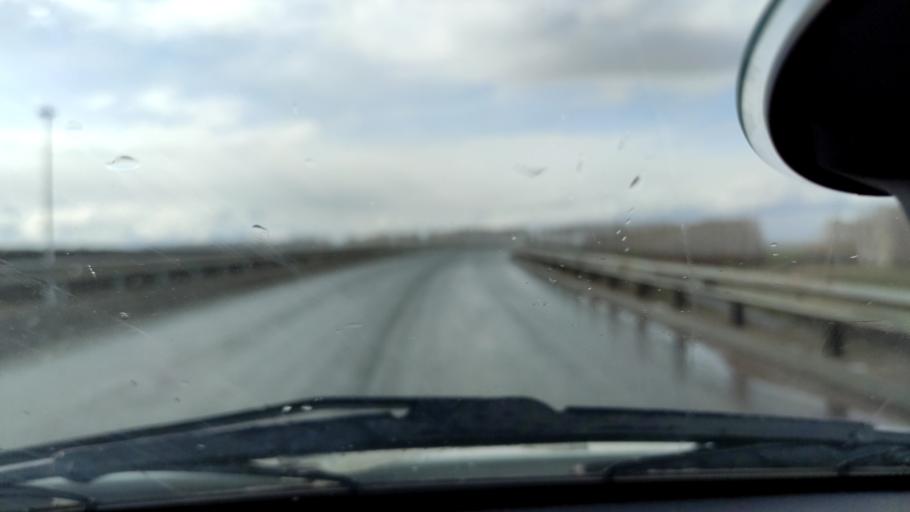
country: RU
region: Bashkortostan
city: Buzdyak
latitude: 54.6449
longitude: 54.5396
